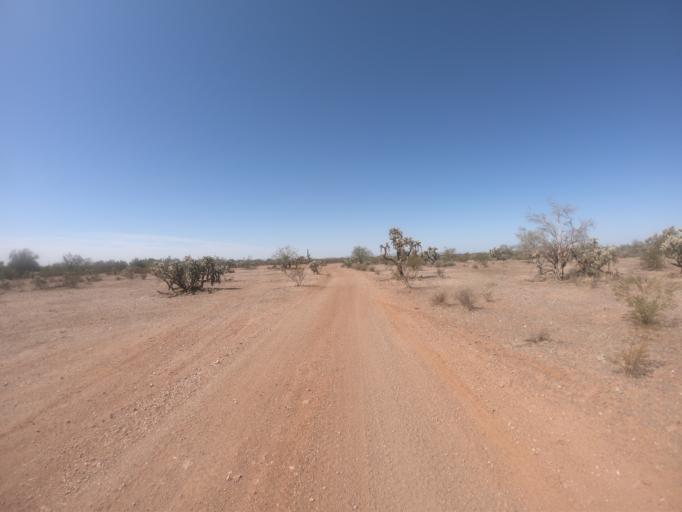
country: US
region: Arizona
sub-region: Pinal County
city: Gold Camp
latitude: 33.2446
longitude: -111.3114
